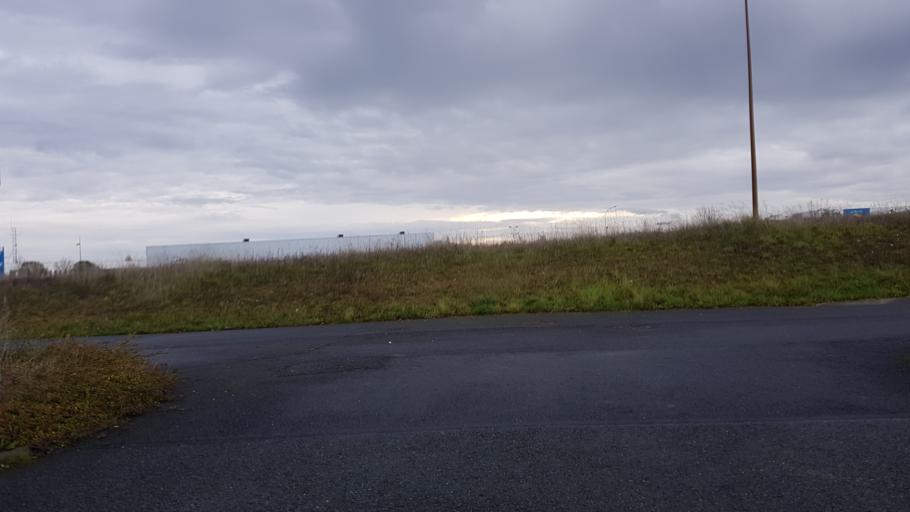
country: FR
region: Poitou-Charentes
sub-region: Departement de la Vienne
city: Chasseneuil-du-Poitou
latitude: 46.6546
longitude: 0.3605
